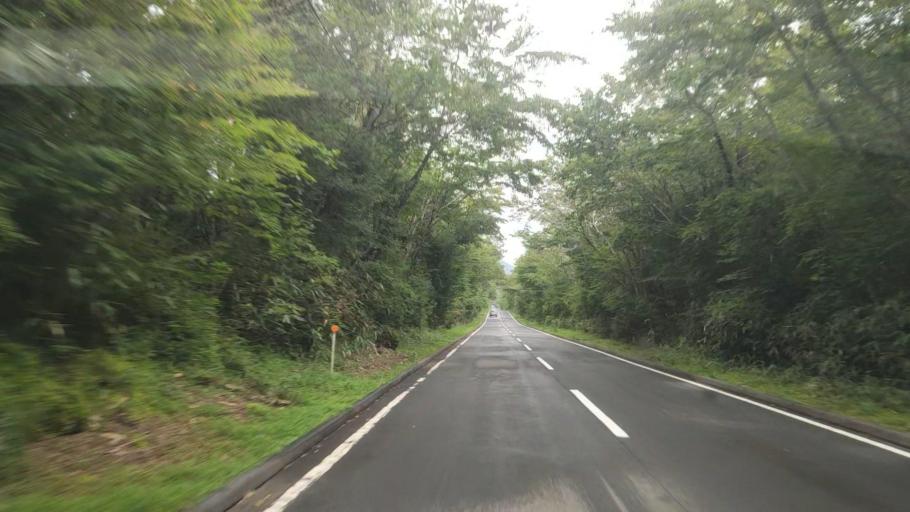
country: JP
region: Shizuoka
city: Gotemba
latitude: 35.2724
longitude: 138.7973
